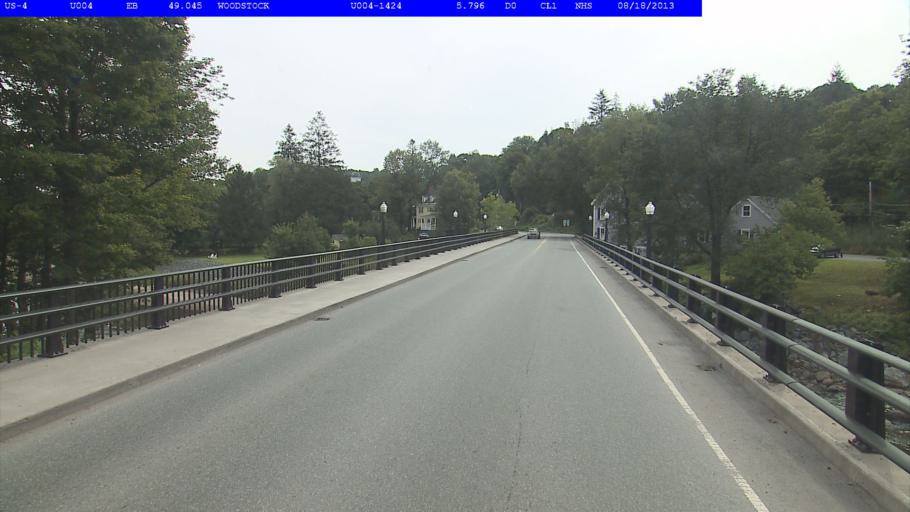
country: US
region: Vermont
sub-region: Windsor County
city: Woodstock
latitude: 43.6223
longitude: -72.5259
